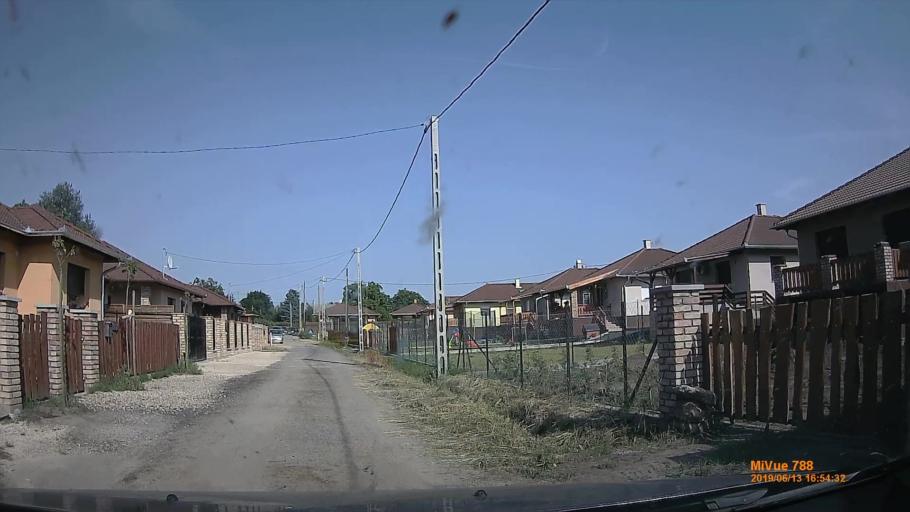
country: HU
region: Pest
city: Gyomro
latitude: 47.4162
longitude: 19.4011
